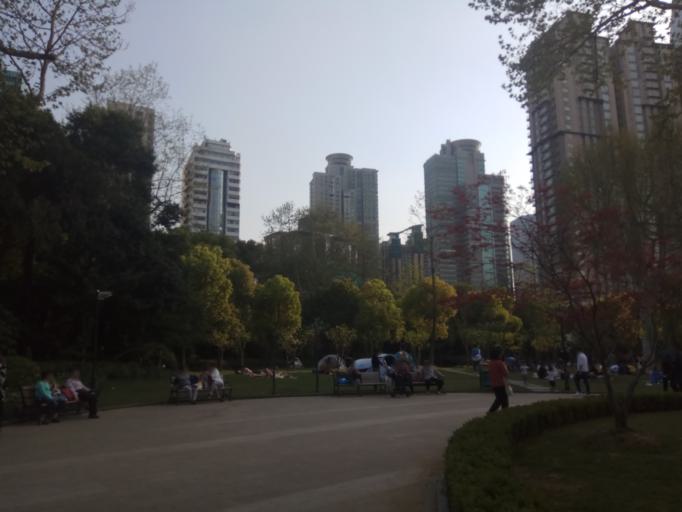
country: CN
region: Shanghai Shi
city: Changning
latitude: 31.2223
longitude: 121.4159
